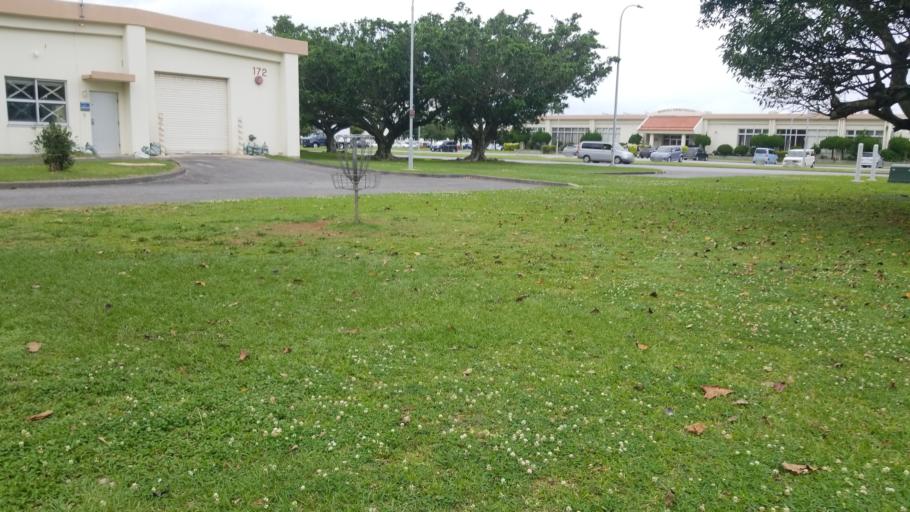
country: JP
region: Okinawa
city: Okinawa
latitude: 26.3377
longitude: 127.7771
